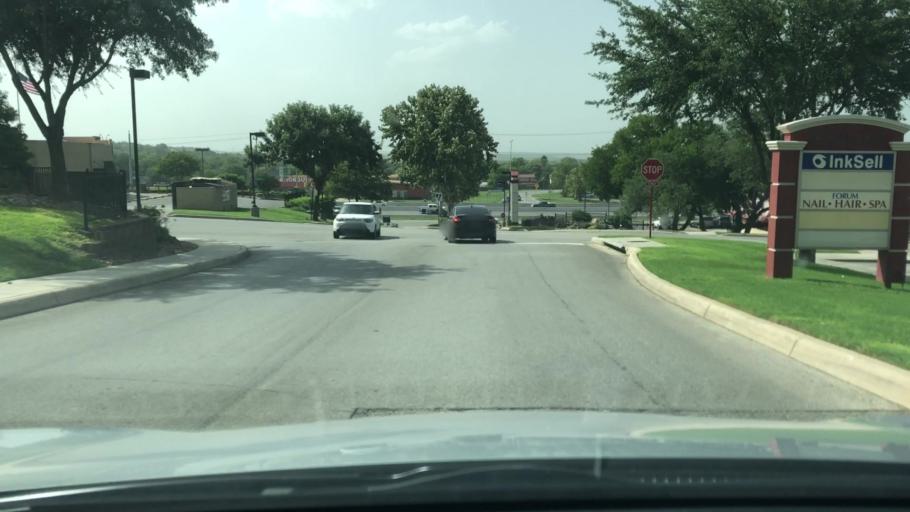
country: US
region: Texas
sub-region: Bexar County
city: Selma
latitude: 29.5755
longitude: -98.3213
